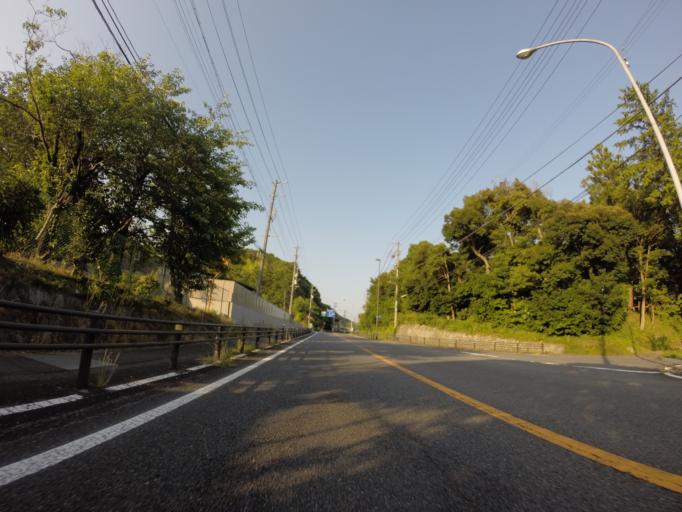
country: JP
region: Shizuoka
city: Kakegawa
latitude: 34.7856
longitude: 138.0634
